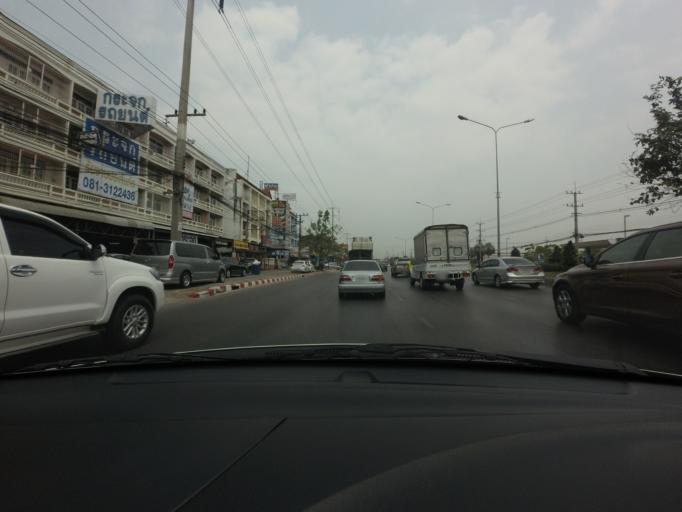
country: TH
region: Bangkok
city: Thawi Watthana
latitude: 13.7518
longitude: 100.3288
